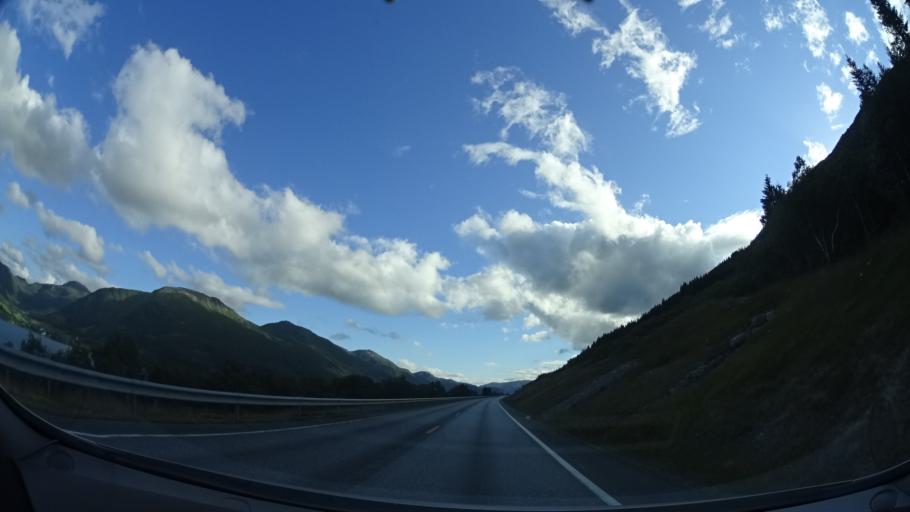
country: NO
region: More og Romsdal
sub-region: Gjemnes
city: Batnfjordsora
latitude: 62.9365
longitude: 7.7326
